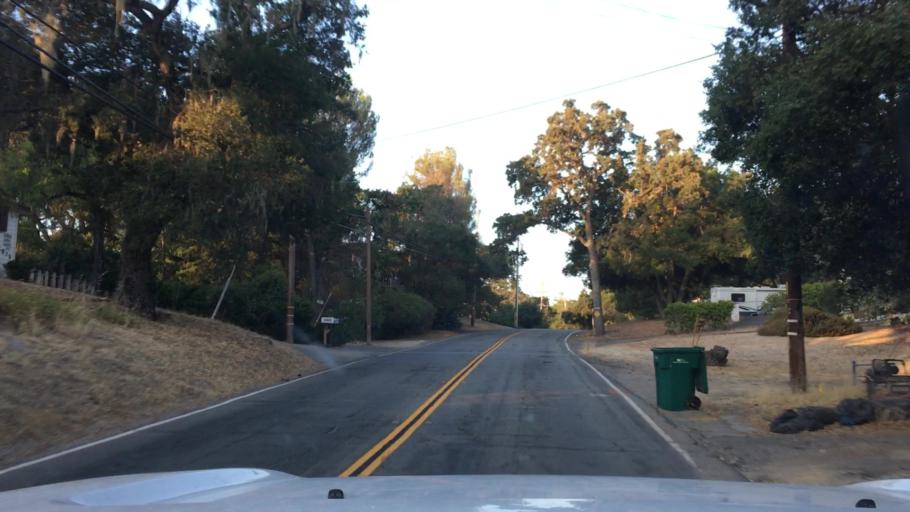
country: US
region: California
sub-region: San Luis Obispo County
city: Atascadero
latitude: 35.4860
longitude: -120.6728
